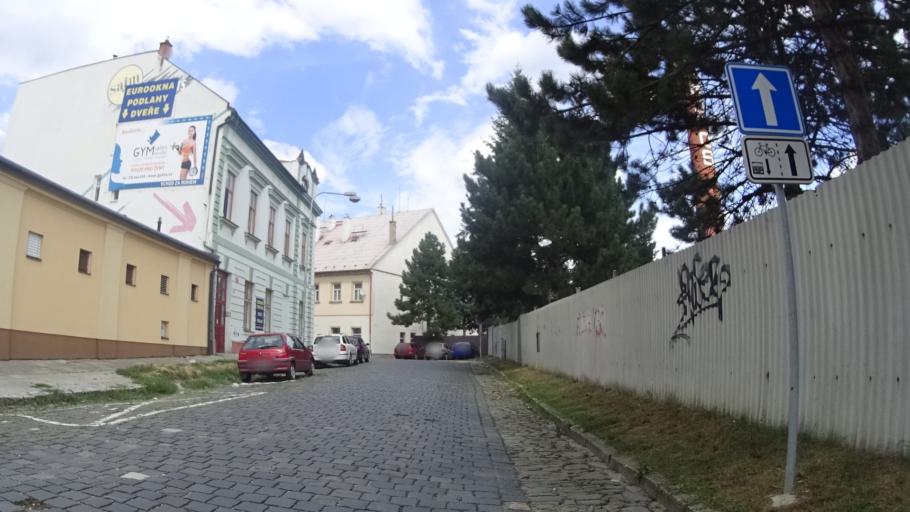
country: CZ
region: Olomoucky
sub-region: Okres Olomouc
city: Olomouc
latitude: 49.6030
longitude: 17.2426
